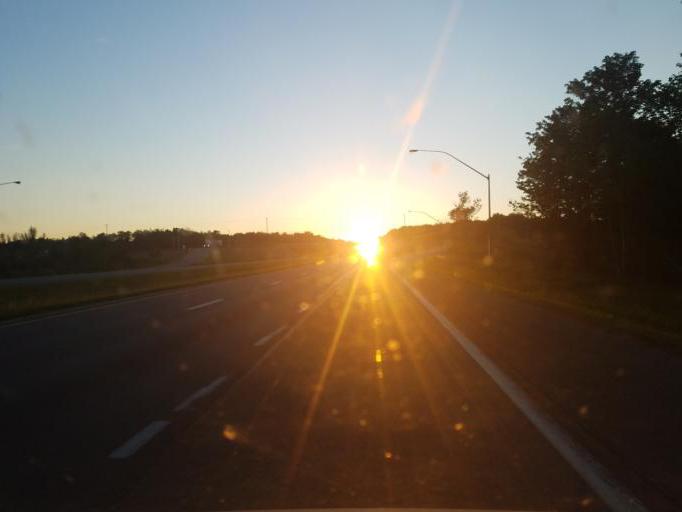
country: US
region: Pennsylvania
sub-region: Erie County
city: Fairview
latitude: 42.0034
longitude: -80.2419
